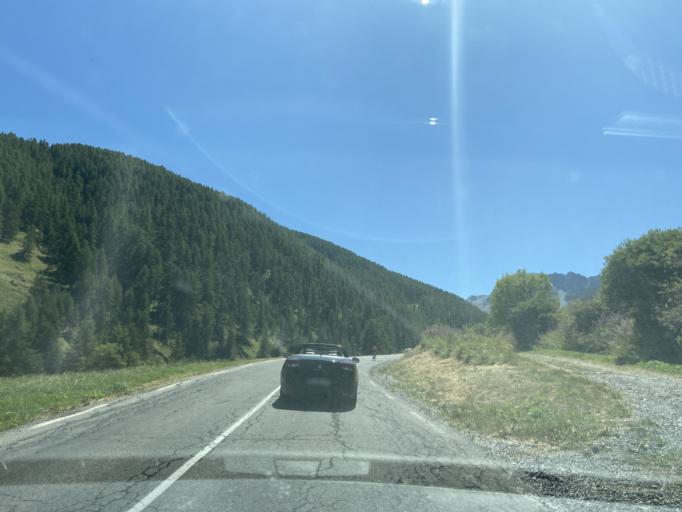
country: FR
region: Provence-Alpes-Cote d'Azur
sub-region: Departement des Hautes-Alpes
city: Guillestre
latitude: 44.5902
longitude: 6.6877
